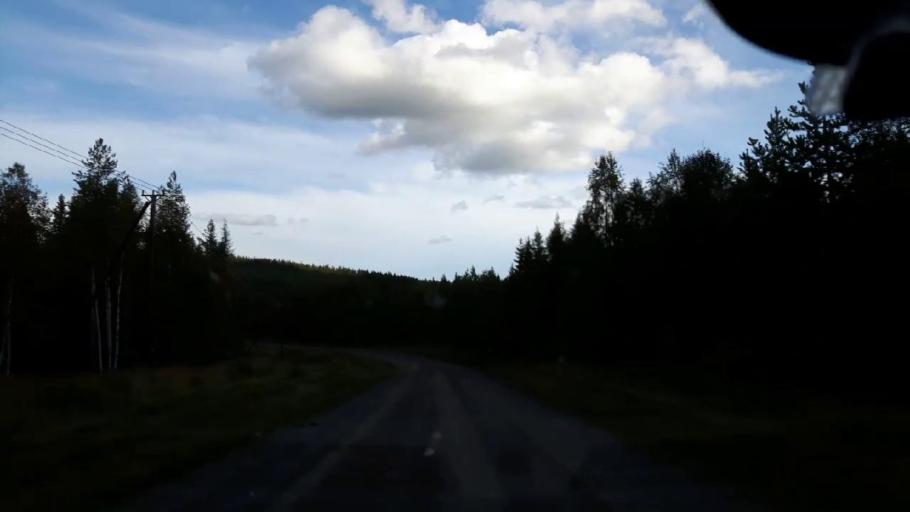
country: SE
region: Jaemtland
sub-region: Ragunda Kommun
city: Hammarstrand
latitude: 63.4225
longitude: 16.0647
